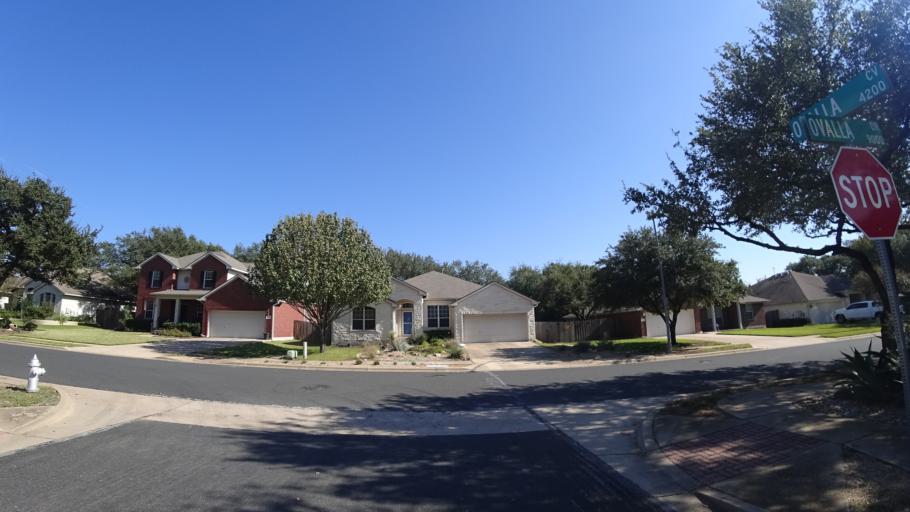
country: US
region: Texas
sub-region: Travis County
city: Shady Hollow
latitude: 30.1971
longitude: -97.8535
